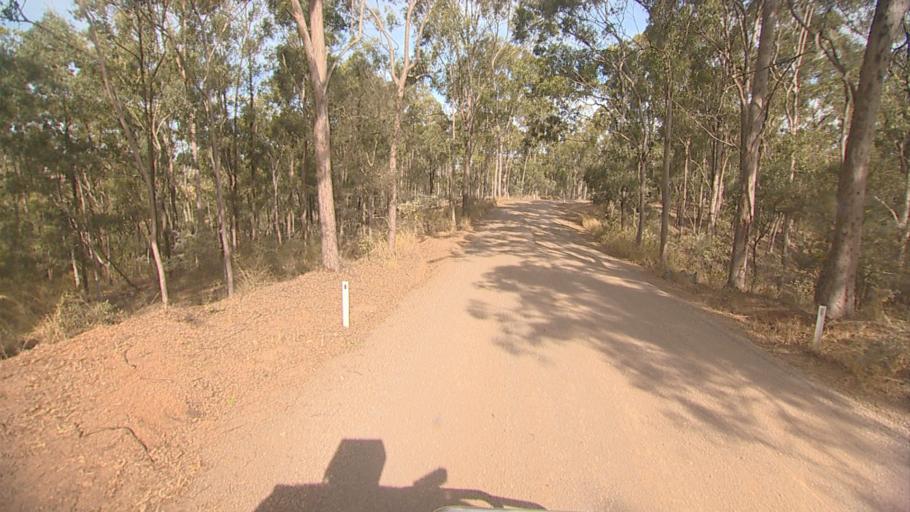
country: AU
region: Queensland
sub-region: Logan
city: Cedar Vale
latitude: -27.8979
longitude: 152.9882
